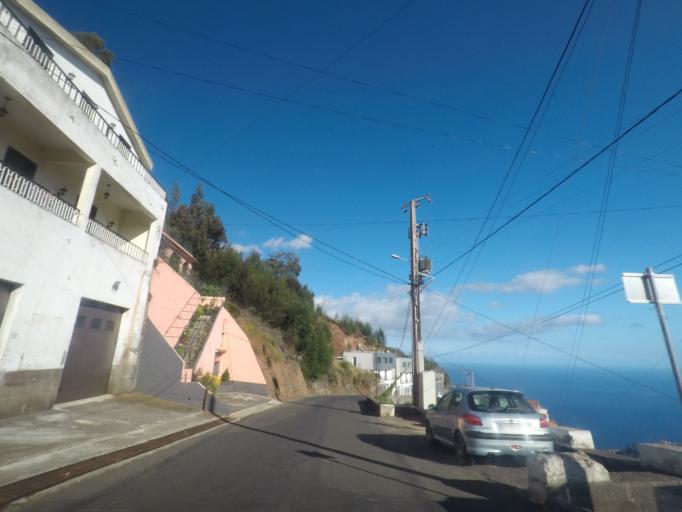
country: PT
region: Madeira
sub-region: Ribeira Brava
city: Campanario
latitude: 32.6651
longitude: -16.9966
